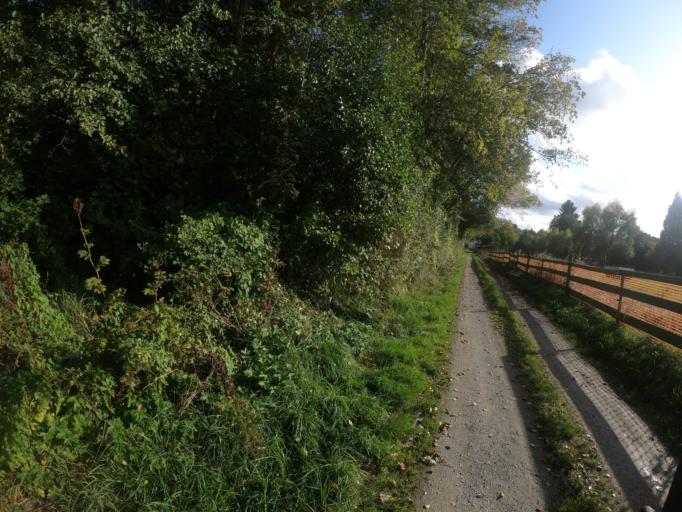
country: DE
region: Hesse
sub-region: Regierungsbezirk Giessen
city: Villmar
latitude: 50.3307
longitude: 8.1816
